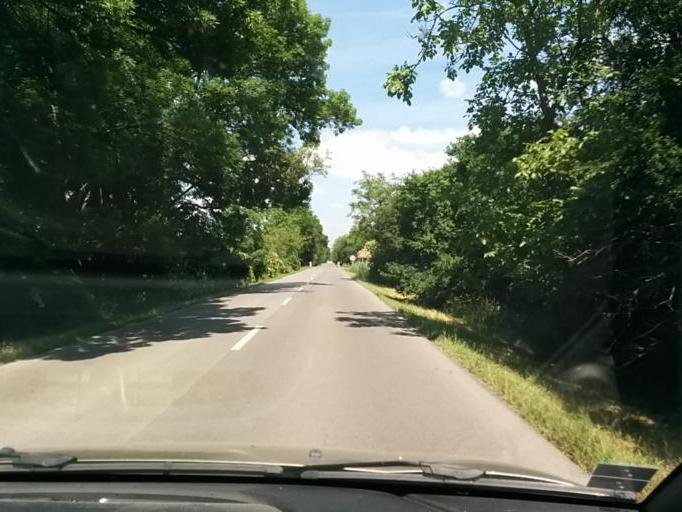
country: SK
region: Trnavsky
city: Sladkovicovo
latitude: 48.2204
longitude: 17.5568
